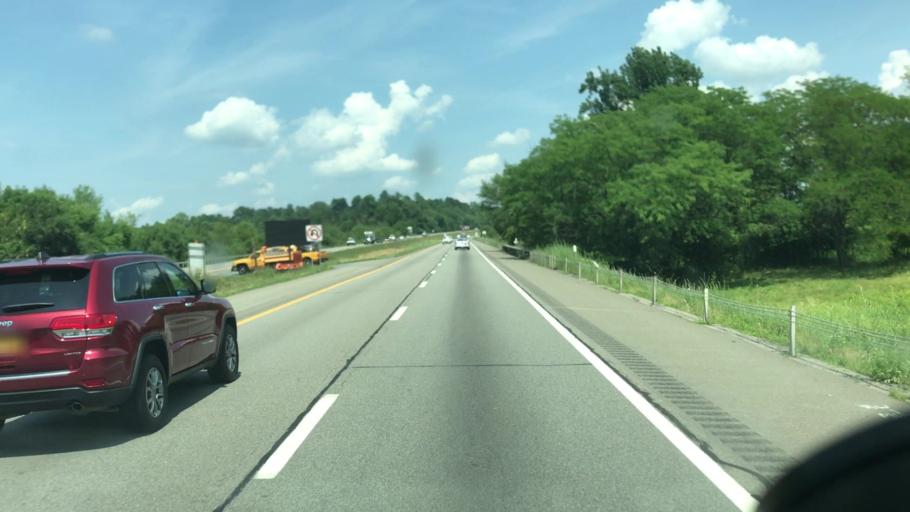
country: US
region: New York
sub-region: Dutchess County
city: Beacon
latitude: 41.5241
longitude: -73.9604
